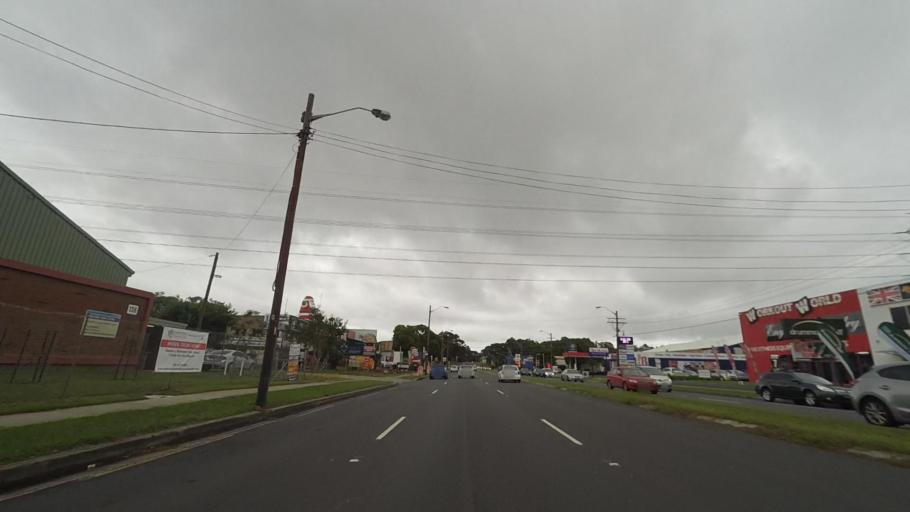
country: AU
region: New South Wales
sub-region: Sutherland Shire
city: Caringbah
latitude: -34.0218
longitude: 151.1213
